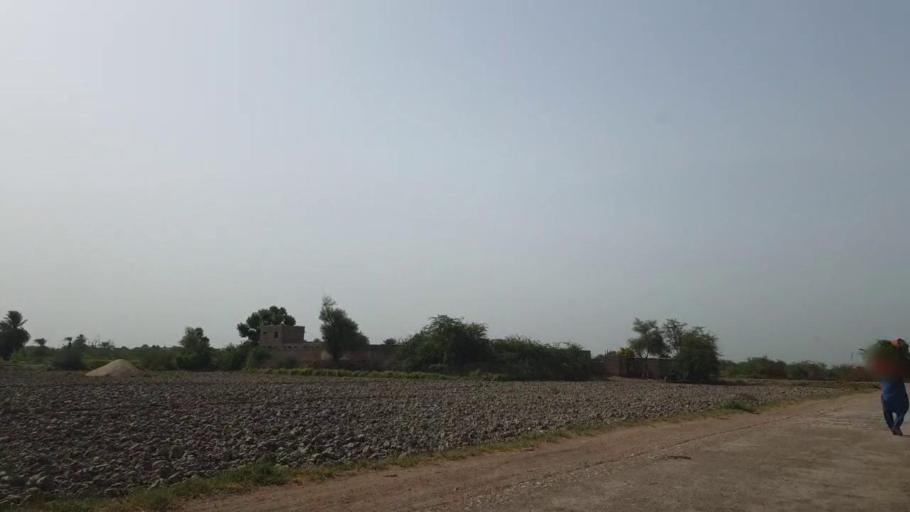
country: PK
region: Sindh
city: Nawabshah
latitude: 26.1146
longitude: 68.4397
